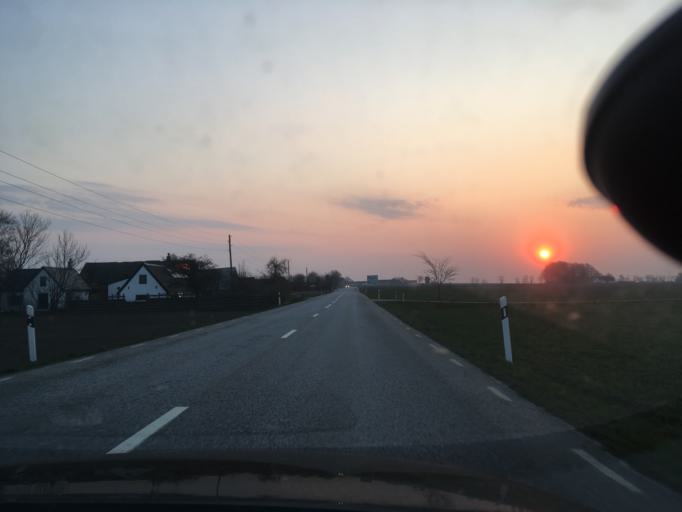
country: SE
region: Skane
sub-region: Tomelilla Kommun
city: Tomelilla
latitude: 55.4793
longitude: 14.0736
